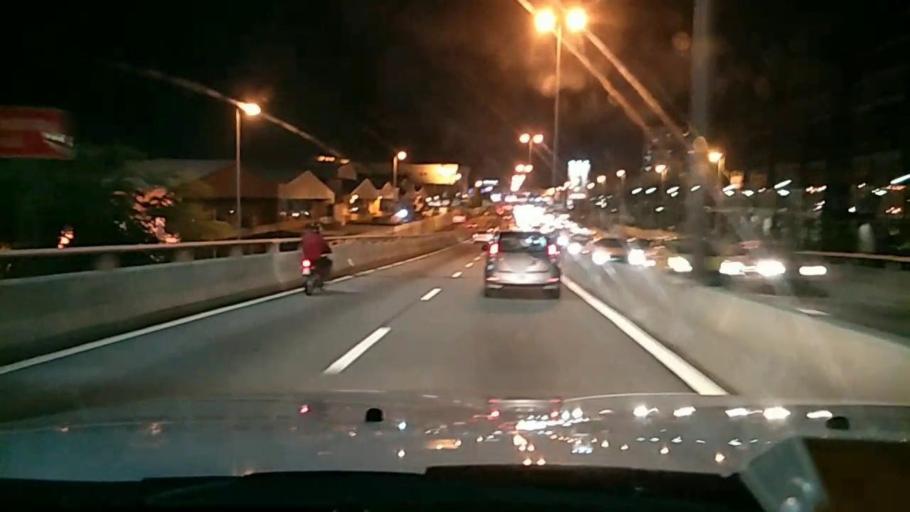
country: MY
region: Selangor
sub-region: Petaling
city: Petaling Jaya
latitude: 3.0860
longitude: 101.6132
